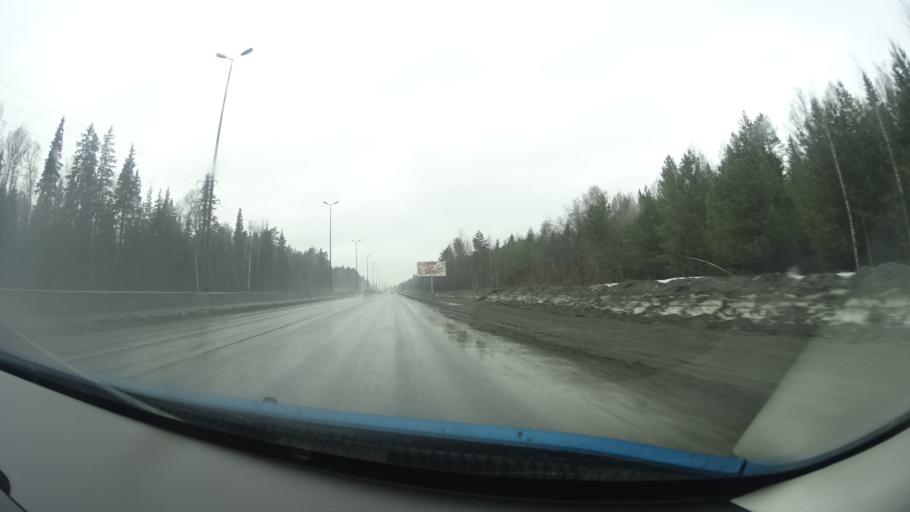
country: RU
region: Perm
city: Kondratovo
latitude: 58.0527
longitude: 56.1469
